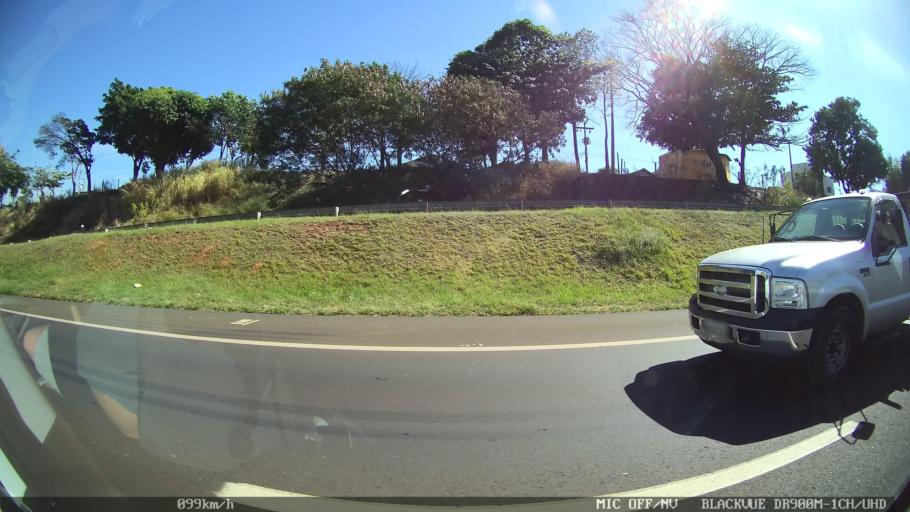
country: BR
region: Sao Paulo
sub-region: Franca
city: Franca
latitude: -20.5309
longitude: -47.4239
